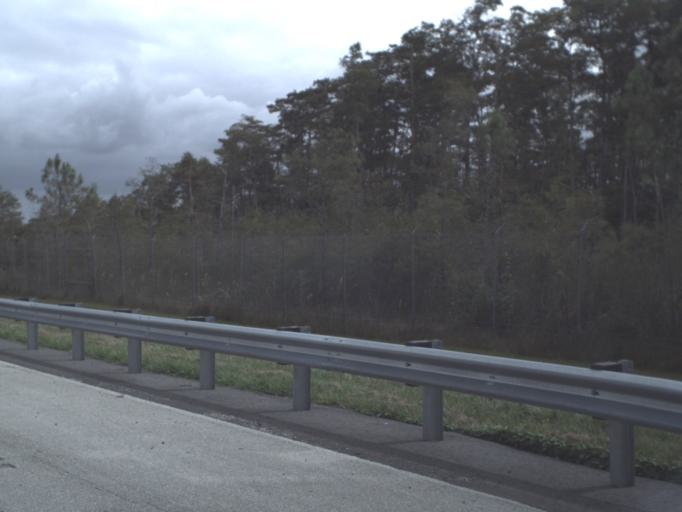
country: US
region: Florida
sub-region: Collier County
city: Immokalee
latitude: 26.1700
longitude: -80.9978
